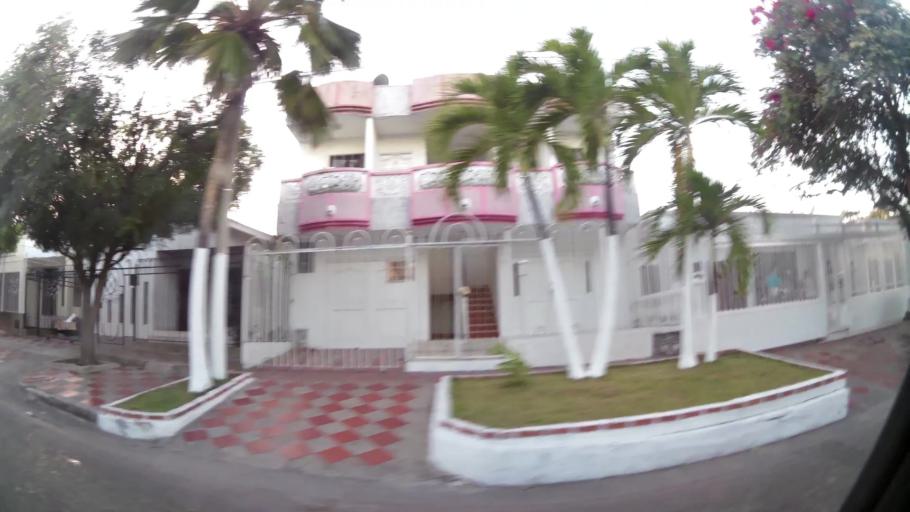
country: CO
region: Atlantico
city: Barranquilla
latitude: 10.9793
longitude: -74.8053
